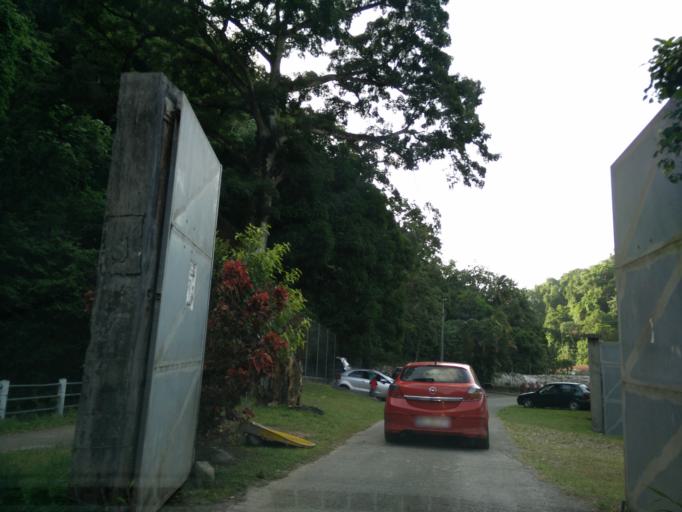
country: MQ
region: Martinique
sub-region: Martinique
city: Basse-Pointe
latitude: 14.8691
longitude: -61.1763
